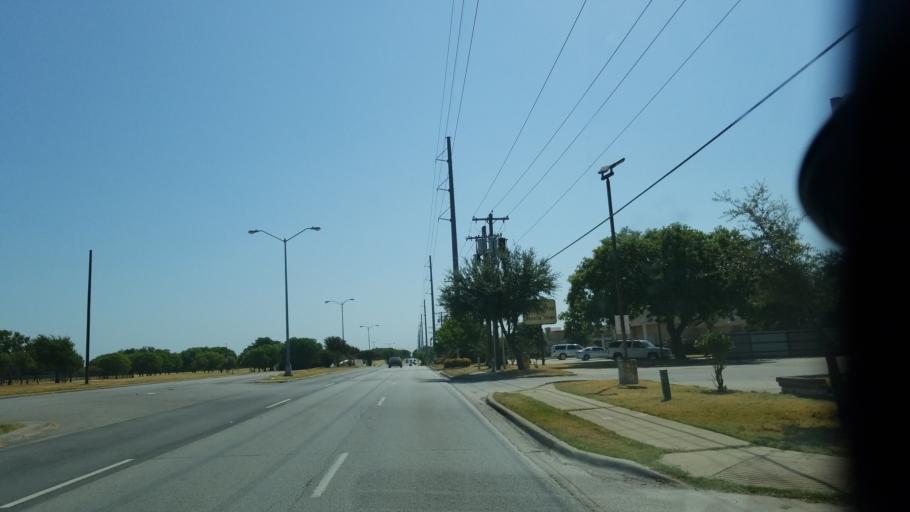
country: US
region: Texas
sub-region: Dallas County
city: Cockrell Hill
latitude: 32.7204
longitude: -96.9075
